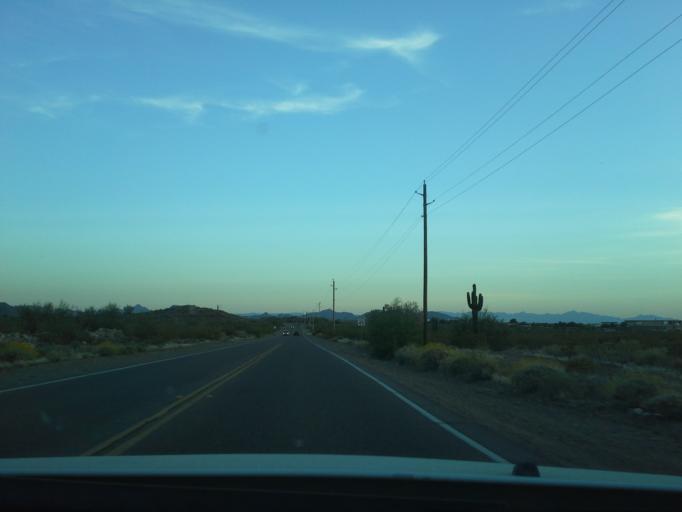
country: US
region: Arizona
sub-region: Maricopa County
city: Cave Creek
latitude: 33.7080
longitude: -112.0657
